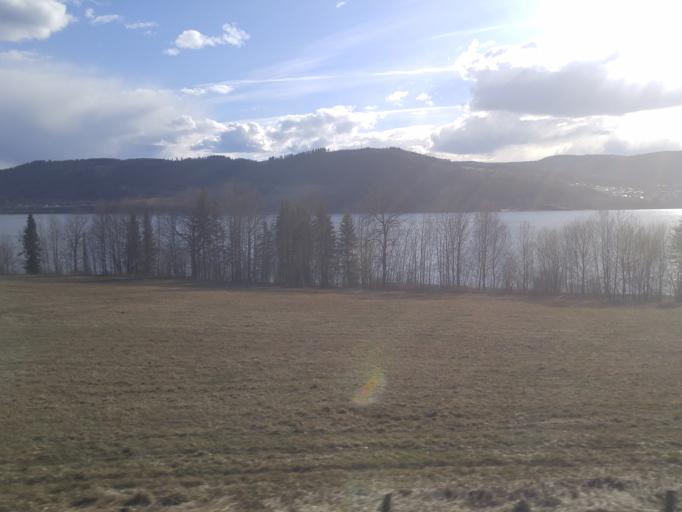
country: NO
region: Hedmark
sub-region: Ringsaker
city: Moelv
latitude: 60.9557
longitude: 10.6708
